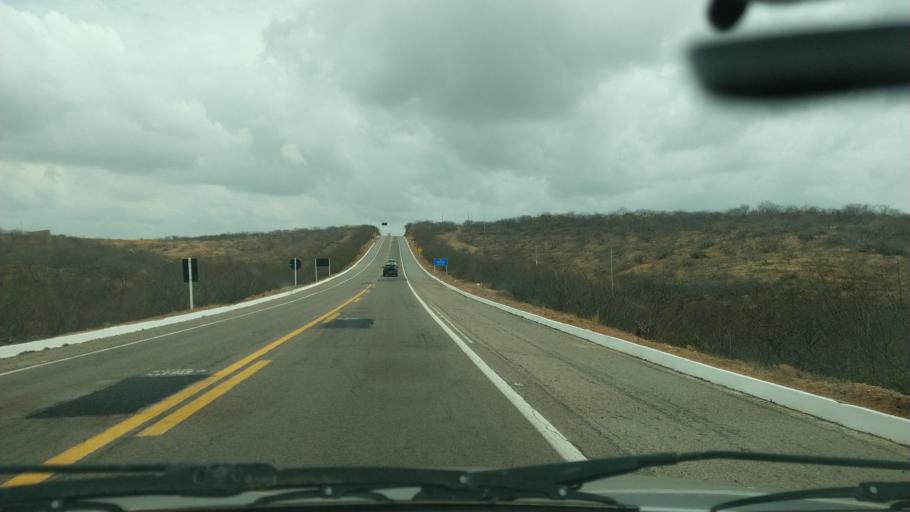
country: BR
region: Rio Grande do Norte
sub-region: Currais Novos
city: Currais Novos
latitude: -6.2199
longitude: -36.4268
